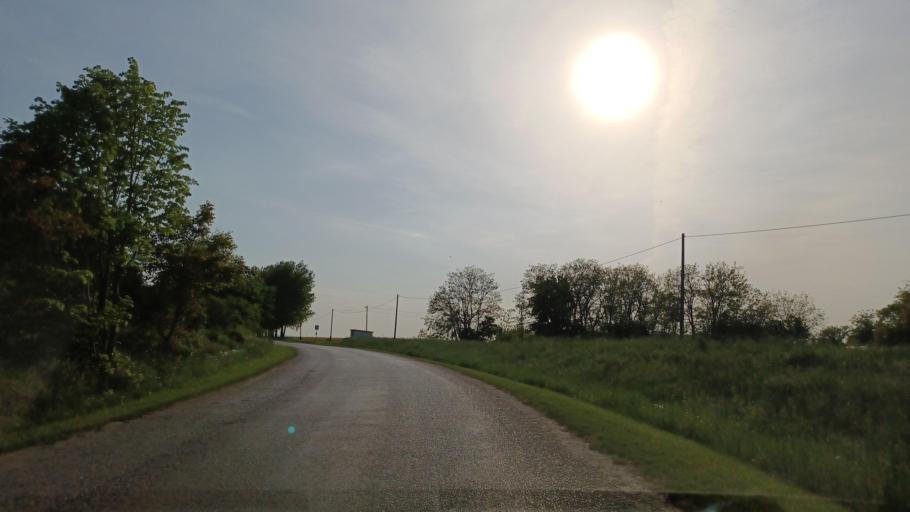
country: HU
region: Baranya
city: Villany
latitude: 45.9554
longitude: 18.3846
